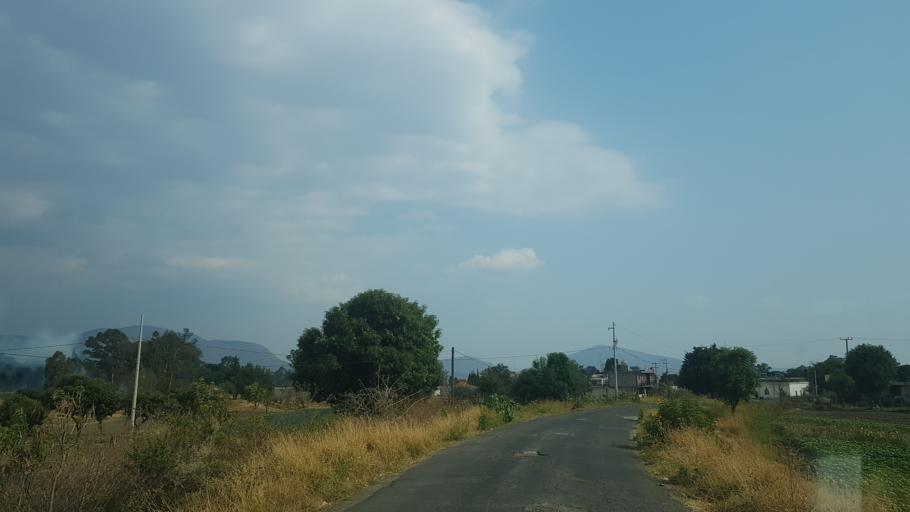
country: MX
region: Puebla
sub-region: Santa Isabel Cholula
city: Santa Ana Acozautla
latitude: 18.9501
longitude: -98.3955
